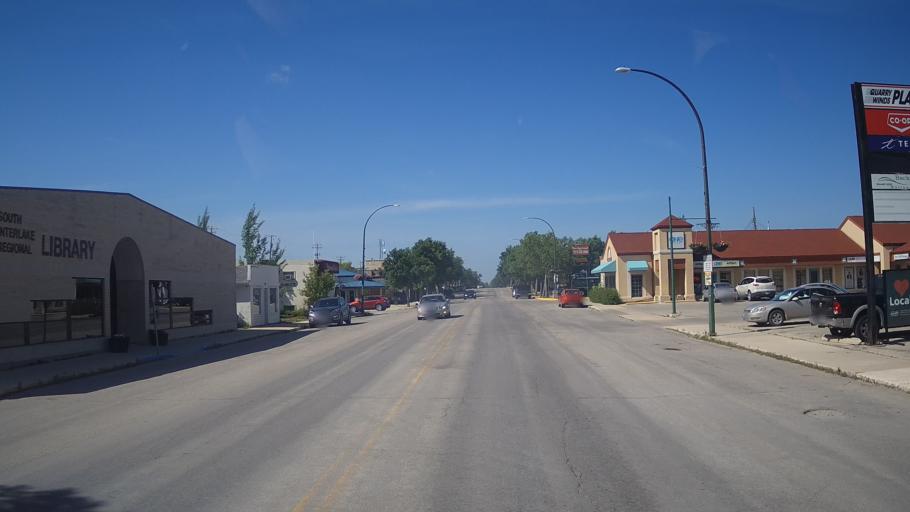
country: CA
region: Manitoba
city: Stonewall
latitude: 50.1325
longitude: -97.3266
